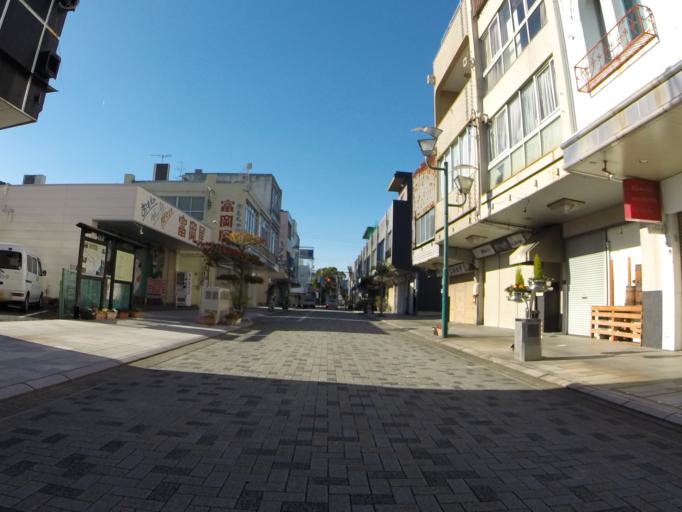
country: JP
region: Shizuoka
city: Shizuoka-shi
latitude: 35.0194
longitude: 138.4826
